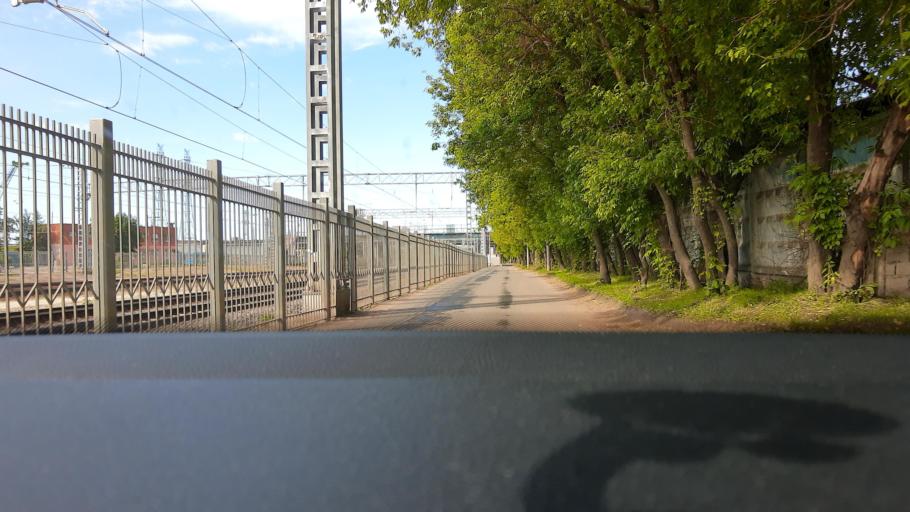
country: RU
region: Moscow
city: Rostokino
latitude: 55.8433
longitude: 37.6710
